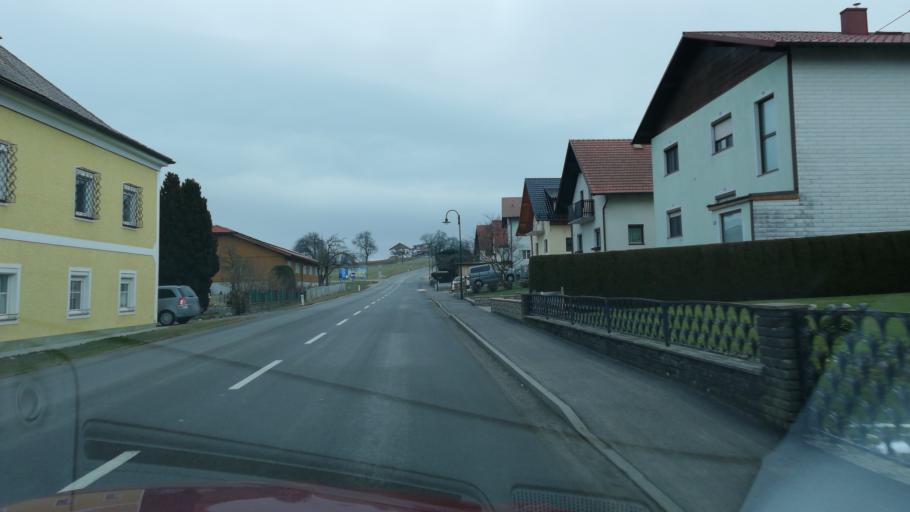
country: AT
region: Upper Austria
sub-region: Politischer Bezirk Vocklabruck
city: Niederthalheim
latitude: 48.1861
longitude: 13.7473
